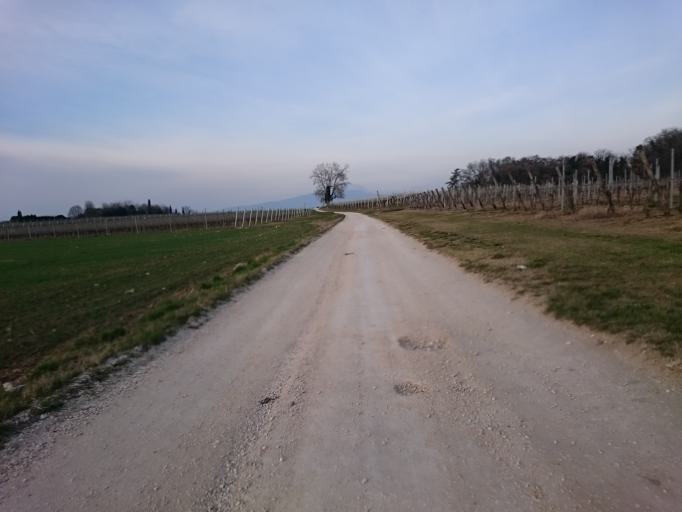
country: IT
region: Veneto
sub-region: Provincia di Verona
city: Cavalcaselle
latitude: 45.4525
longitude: 10.7337
